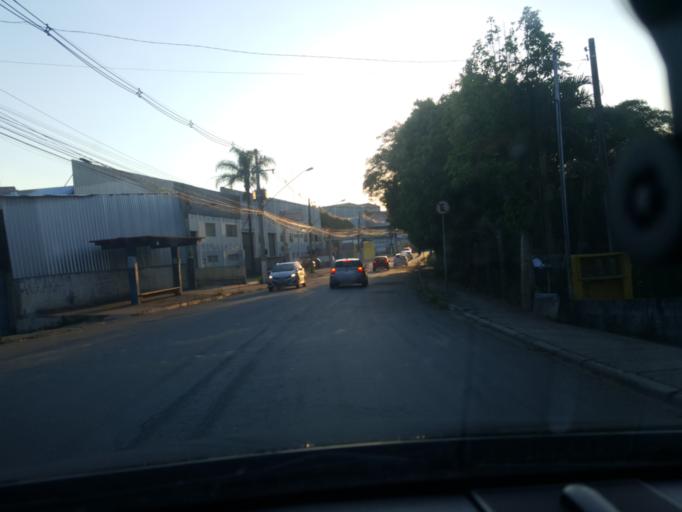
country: BR
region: Sao Paulo
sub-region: Cajamar
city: Cajamar
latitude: -23.3823
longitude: -46.8591
